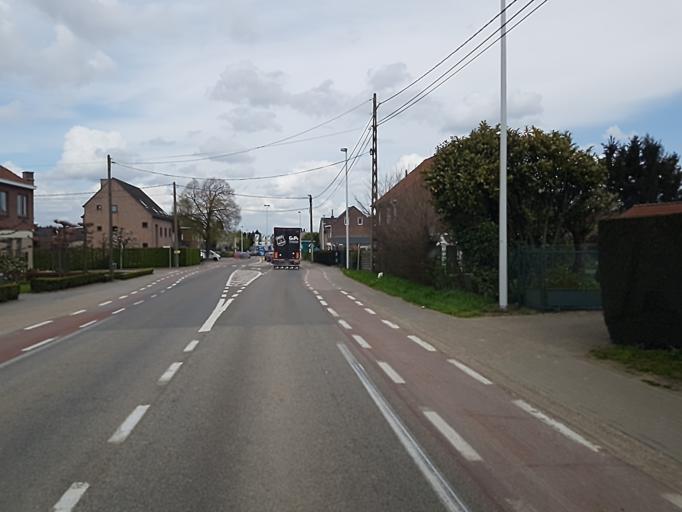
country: BE
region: Flanders
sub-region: Provincie Limburg
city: Lanaken
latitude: 50.8591
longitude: 5.6251
